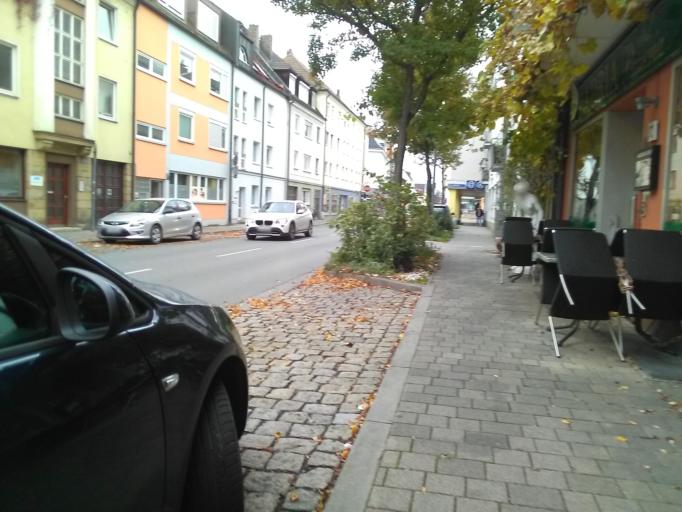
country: DE
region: Bavaria
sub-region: Upper Franconia
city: Bayreuth
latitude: 49.9489
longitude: 11.5768
